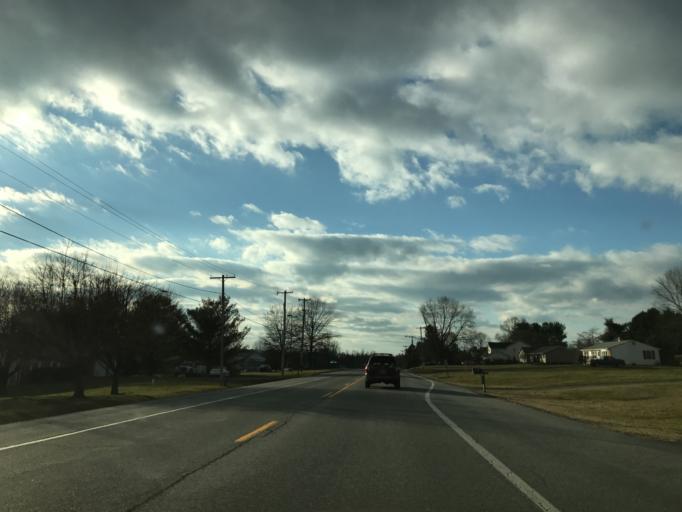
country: US
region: Maryland
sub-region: Cecil County
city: Rising Sun
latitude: 39.6924
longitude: -76.0545
